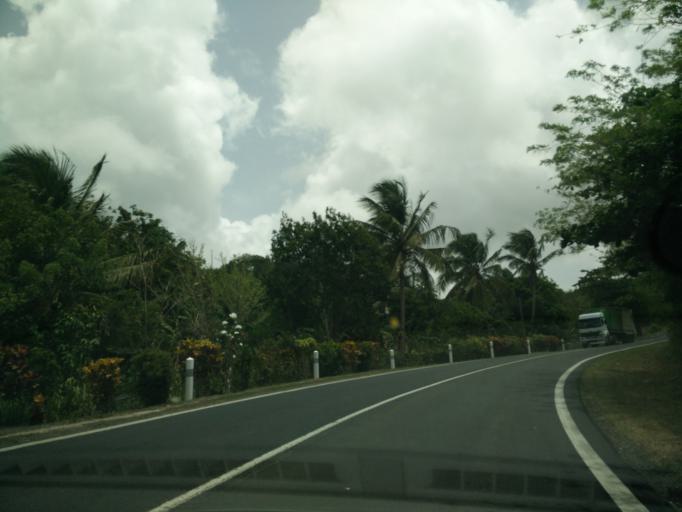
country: GP
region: Guadeloupe
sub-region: Guadeloupe
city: Petit-Canal
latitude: 16.3524
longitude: -61.4563
